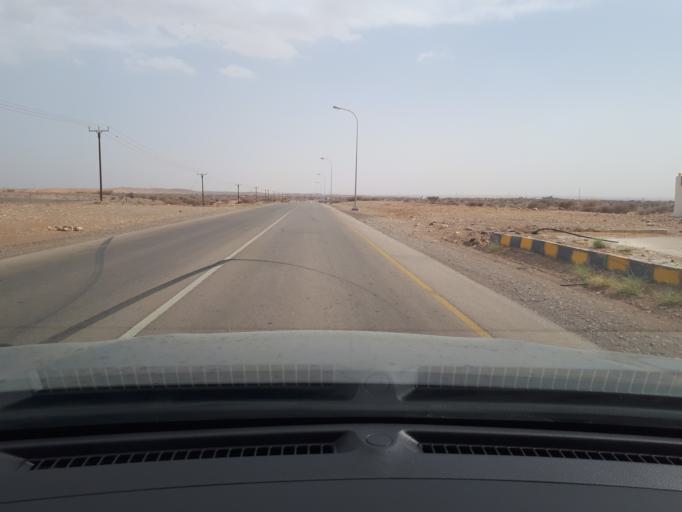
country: OM
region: Ash Sharqiyah
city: Badiyah
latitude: 22.5127
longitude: 58.9479
